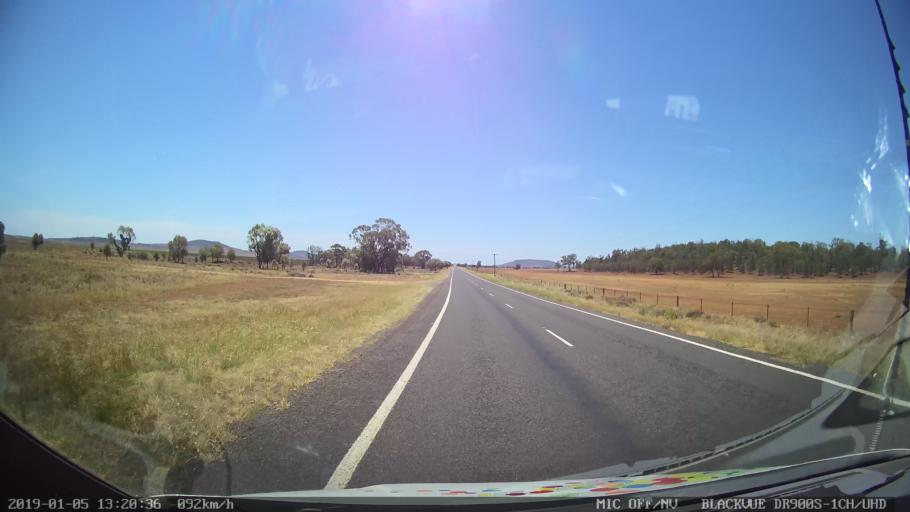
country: AU
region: New South Wales
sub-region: Gunnedah
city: Gunnedah
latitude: -31.1012
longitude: 149.9377
